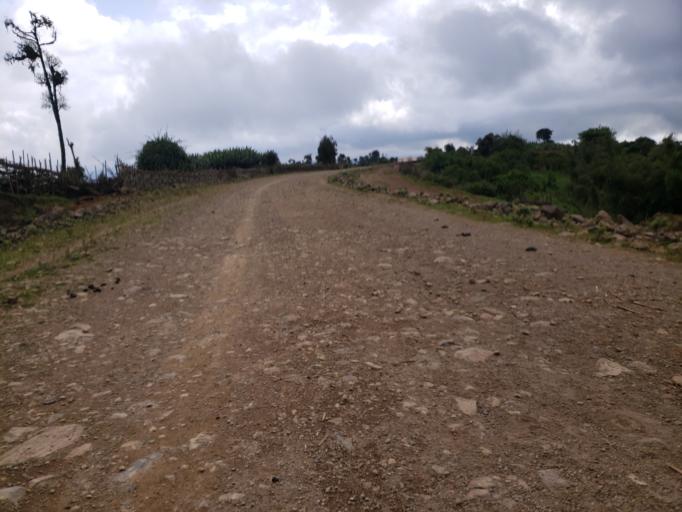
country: ET
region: Oromiya
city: Dodola
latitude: 6.7032
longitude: 39.3732
